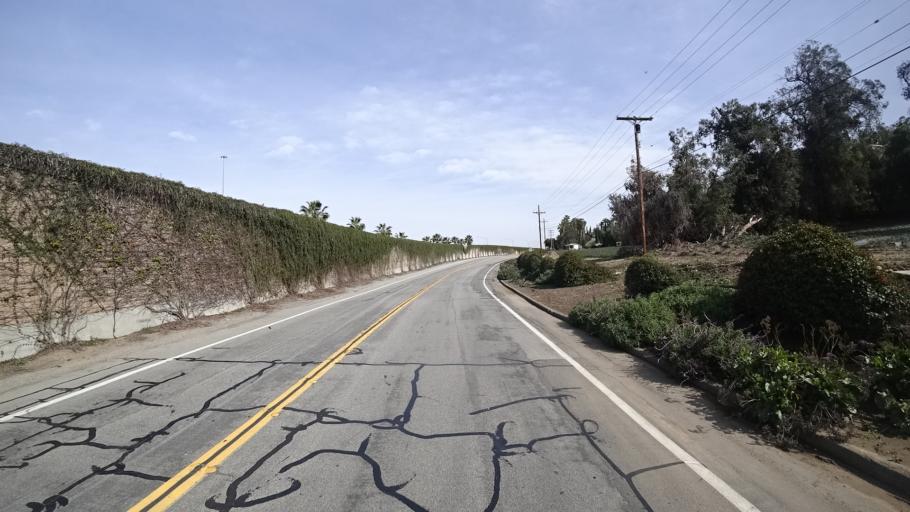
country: US
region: California
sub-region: Orange County
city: Villa Park
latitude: 33.8427
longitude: -117.8288
